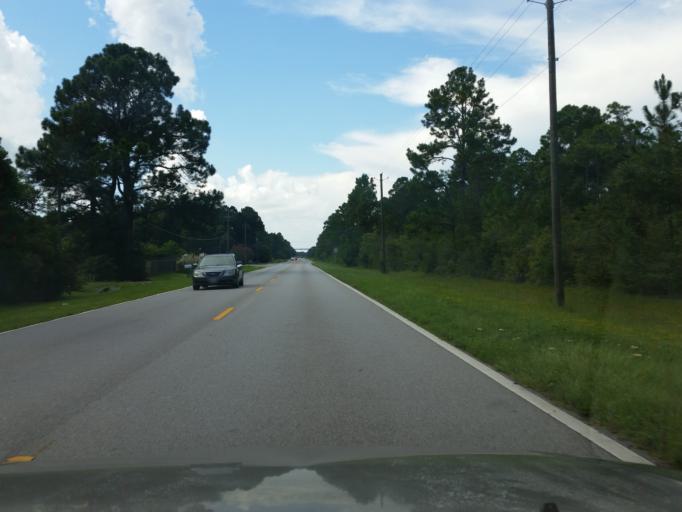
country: US
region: Florida
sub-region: Escambia County
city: Myrtle Grove
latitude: 30.3880
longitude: -87.4022
